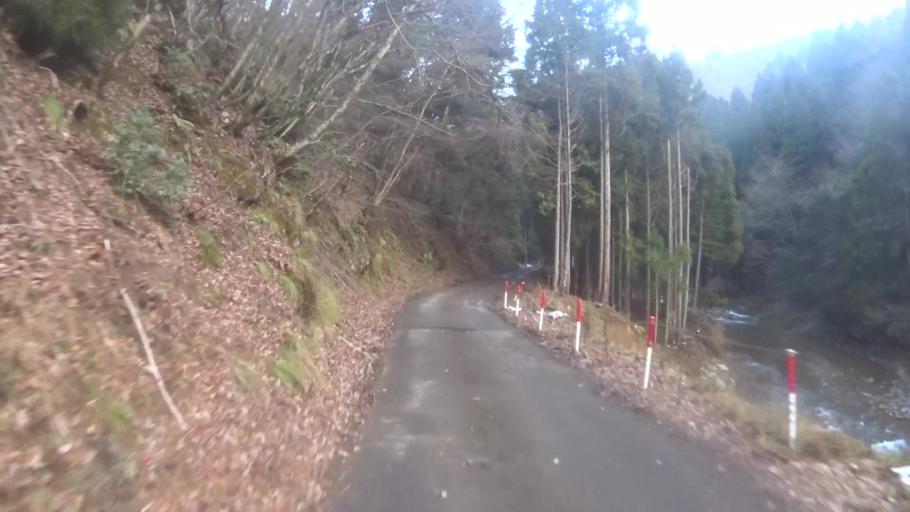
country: JP
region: Kyoto
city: Maizuru
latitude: 35.3961
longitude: 135.4905
